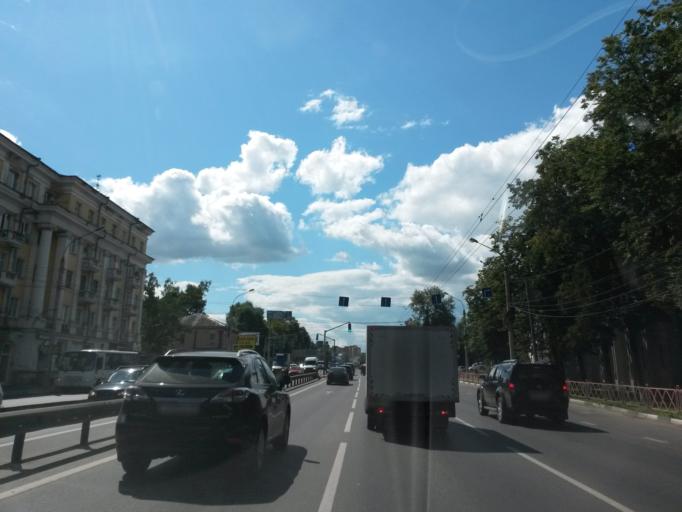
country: RU
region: Jaroslavl
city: Yaroslavl
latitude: 57.6061
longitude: 39.8790
